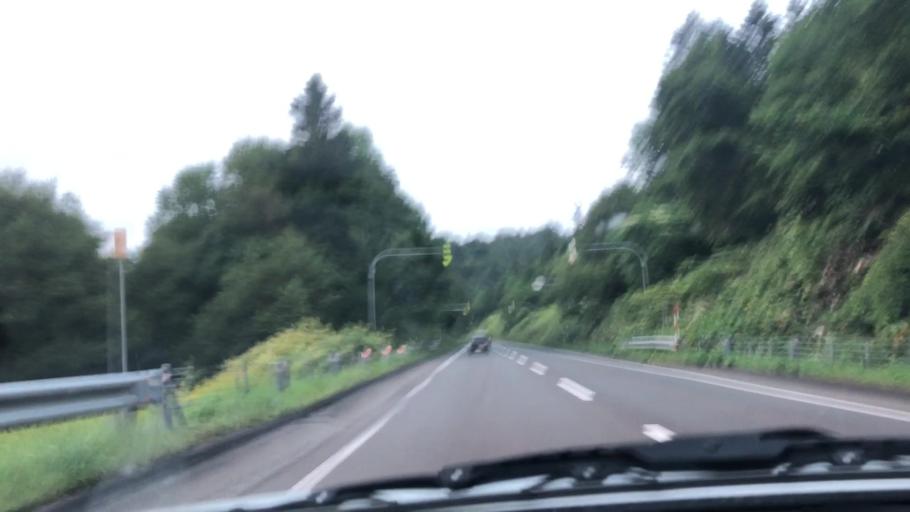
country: JP
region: Hokkaido
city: Iwamizawa
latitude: 42.9004
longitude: 142.1266
